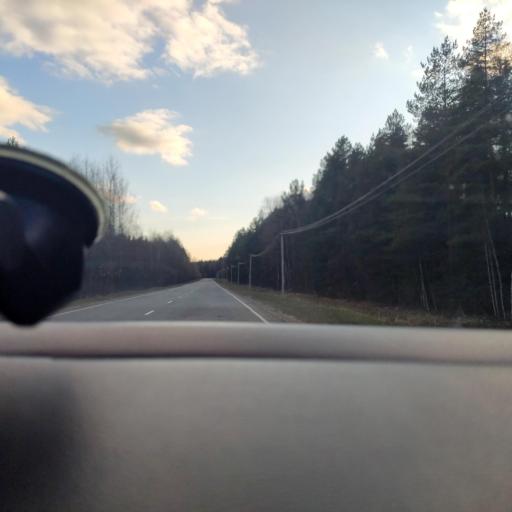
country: RU
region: Moskovskaya
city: Shaturtorf
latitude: 55.4531
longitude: 39.4480
